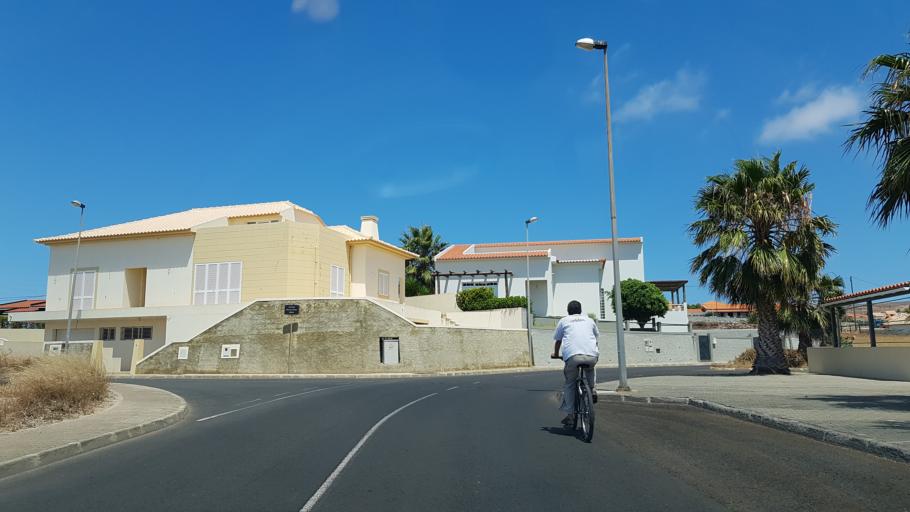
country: PT
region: Madeira
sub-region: Porto Santo
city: Vila de Porto Santo
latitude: 33.0550
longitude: -16.3563
